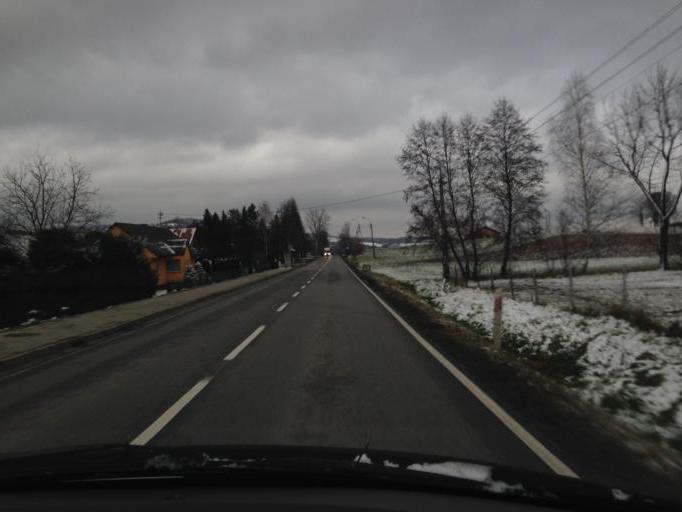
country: PL
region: Lesser Poland Voivodeship
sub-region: Powiat tarnowski
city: Janowice
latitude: 49.8524
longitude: 20.8499
